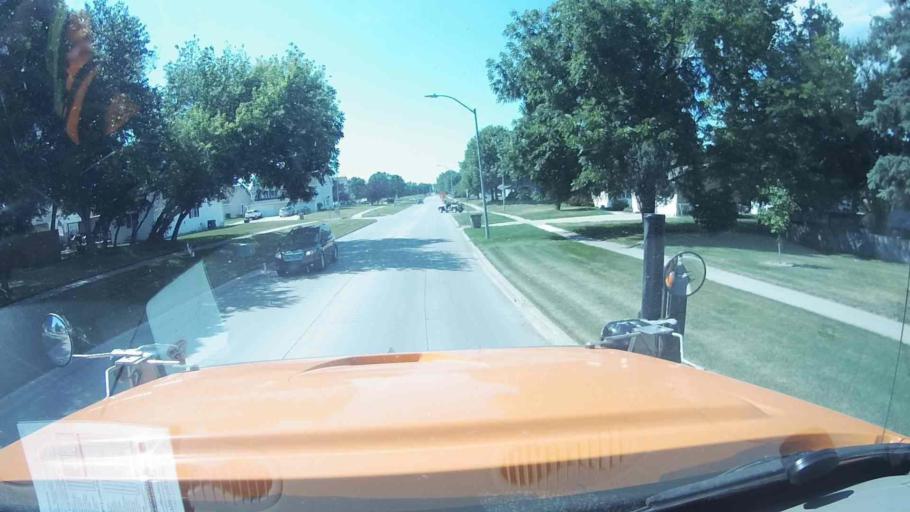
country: US
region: Iowa
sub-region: Polk County
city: Altoona
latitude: 41.6553
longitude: -93.4694
